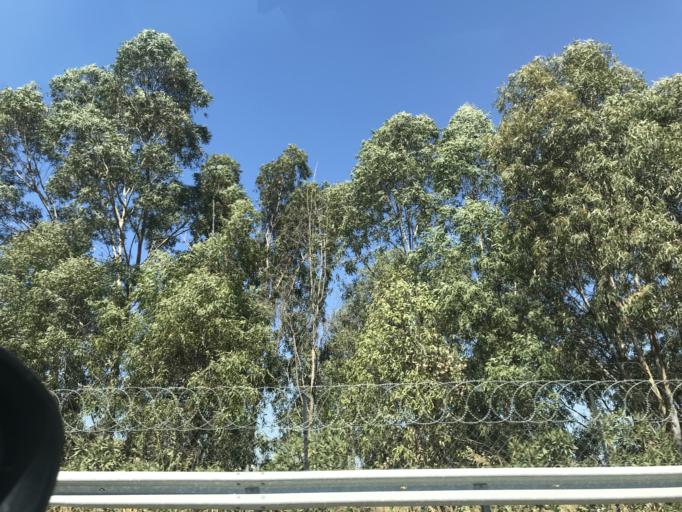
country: TR
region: Aydin
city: Aydin
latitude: 37.8241
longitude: 27.8392
